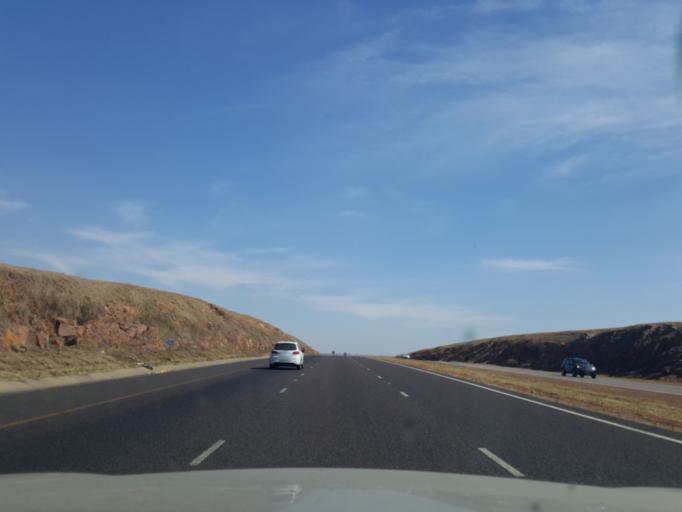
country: ZA
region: Mpumalanga
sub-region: Nkangala District Municipality
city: Middelburg
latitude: -25.8178
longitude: 29.5891
